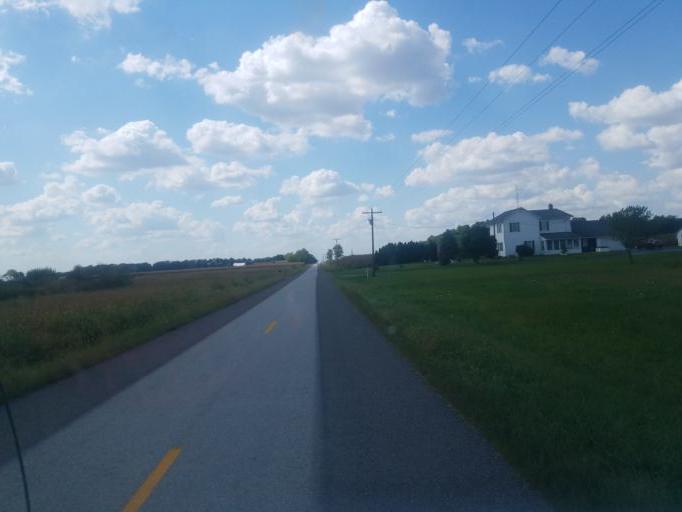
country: US
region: Ohio
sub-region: Auglaize County
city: Wapakoneta
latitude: 40.6532
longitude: -84.2598
